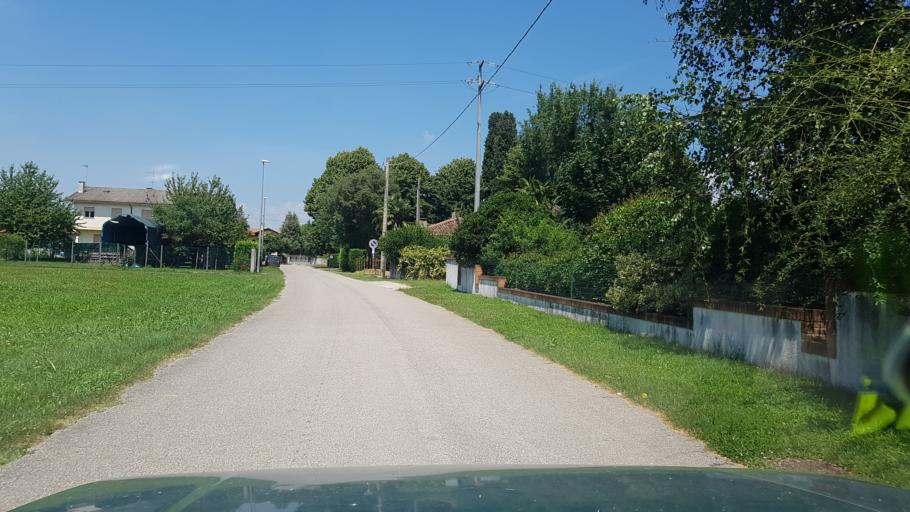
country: IT
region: Friuli Venezia Giulia
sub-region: Provincia di Gorizia
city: Farra d'Isonzo
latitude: 45.9126
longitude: 13.5362
